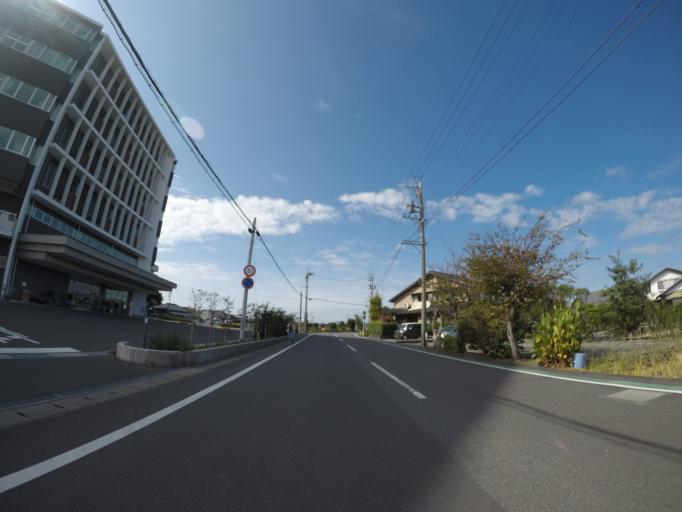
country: JP
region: Shizuoka
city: Fujieda
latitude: 34.8301
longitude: 138.2876
